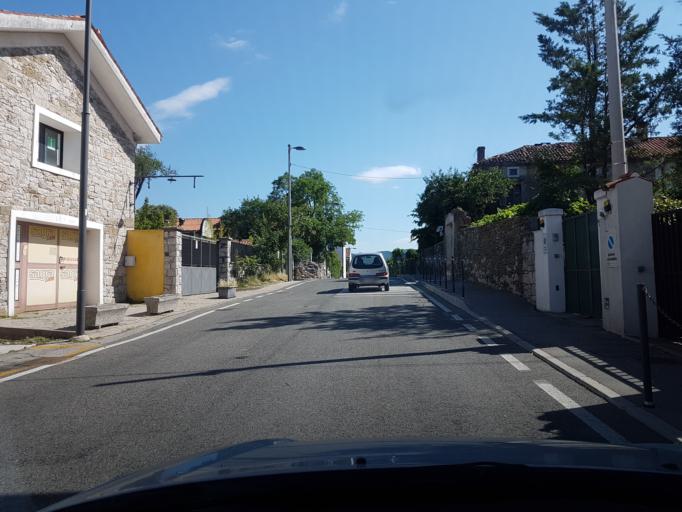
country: IT
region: Friuli Venezia Giulia
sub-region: Provincia di Trieste
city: Prosecco-Contovello
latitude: 45.7061
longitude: 13.7323
